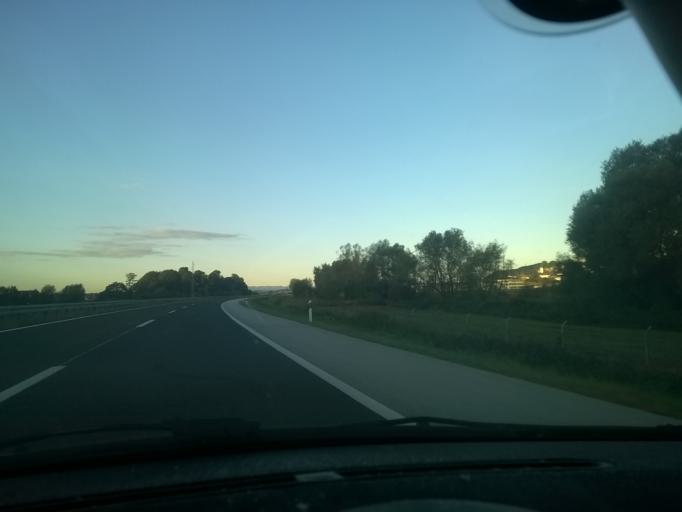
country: HR
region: Krapinsko-Zagorska
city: Zabok
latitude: 46.0323
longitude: 15.9236
